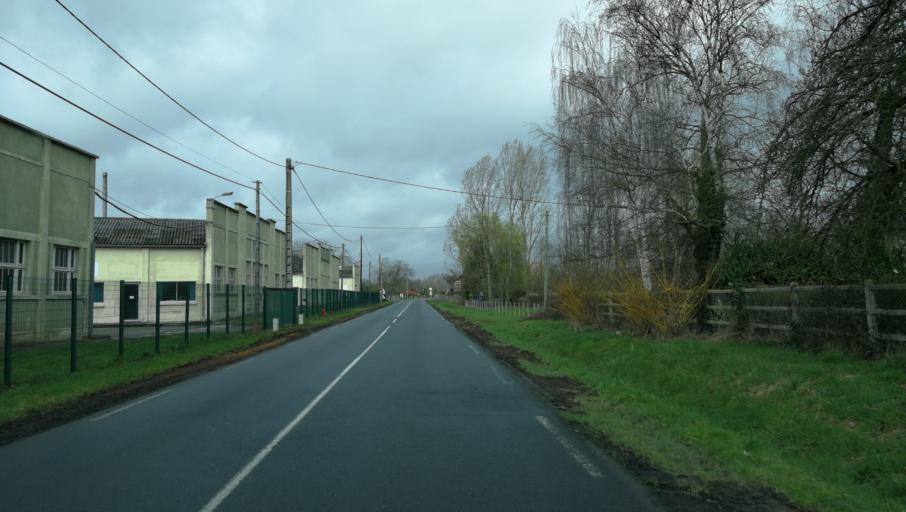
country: FR
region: Haute-Normandie
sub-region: Departement de l'Eure
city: Brionne
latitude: 49.2065
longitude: 0.7116
